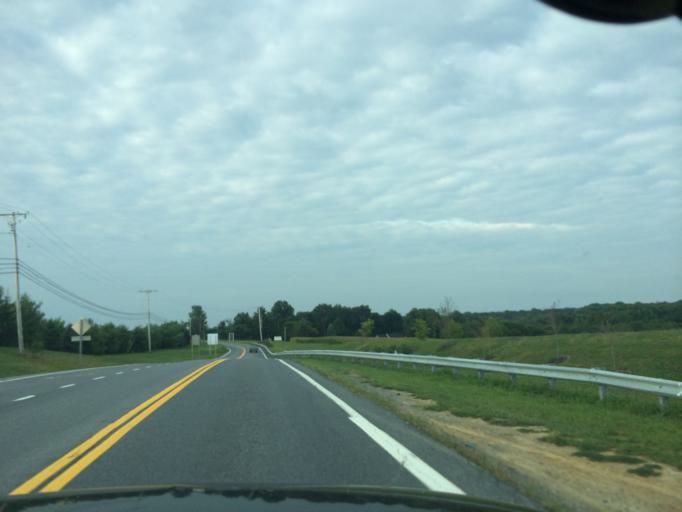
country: US
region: Maryland
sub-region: Carroll County
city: Sykesville
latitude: 39.3885
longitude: -77.0189
